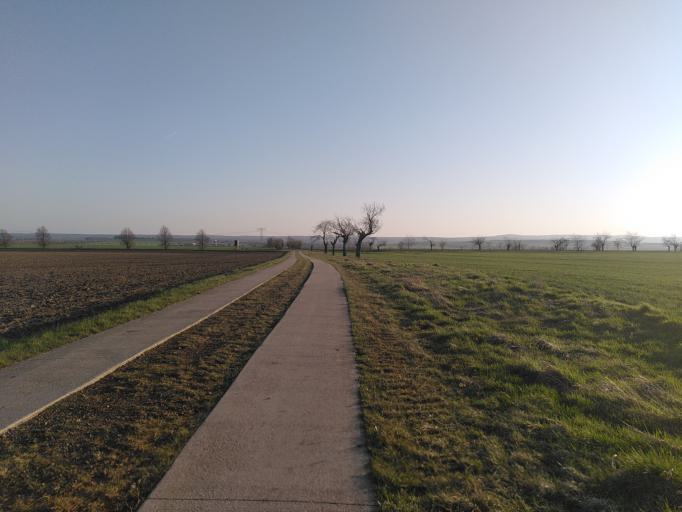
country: DE
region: Saxony-Anhalt
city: Gatersleben
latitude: 51.7997
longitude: 11.2596
